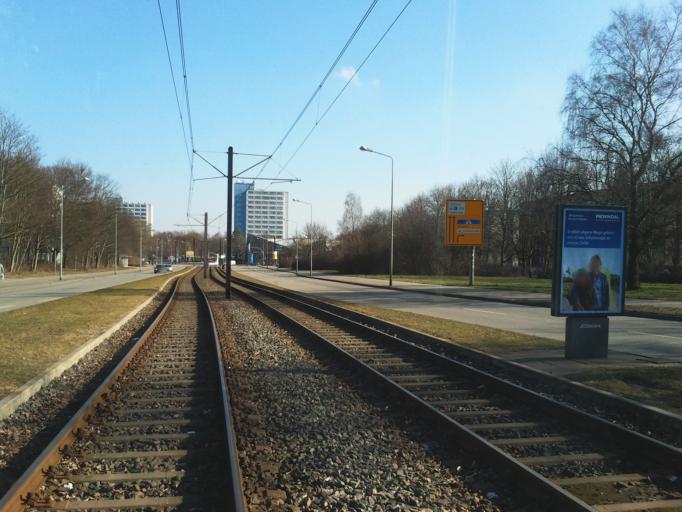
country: DE
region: Mecklenburg-Vorpommern
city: Rostock
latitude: 54.0721
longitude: 12.1128
